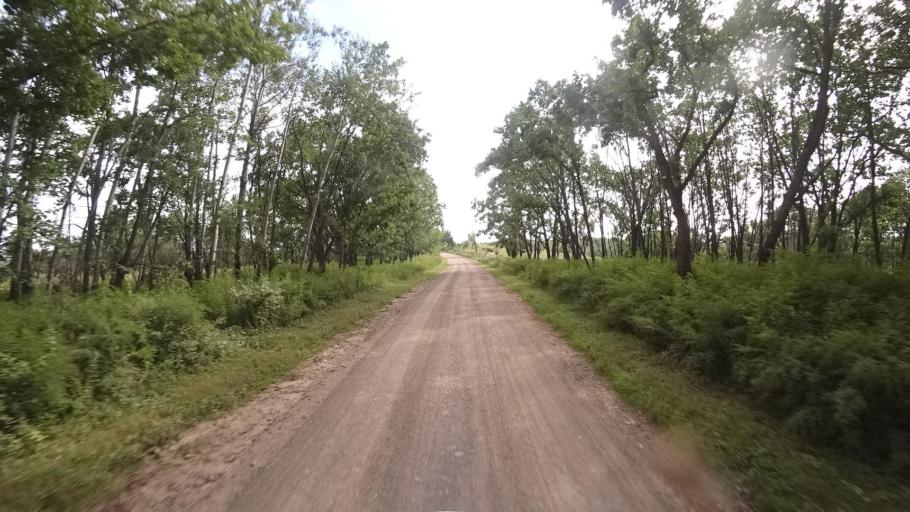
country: RU
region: Primorskiy
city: Dostoyevka
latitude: 44.3611
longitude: 133.5217
